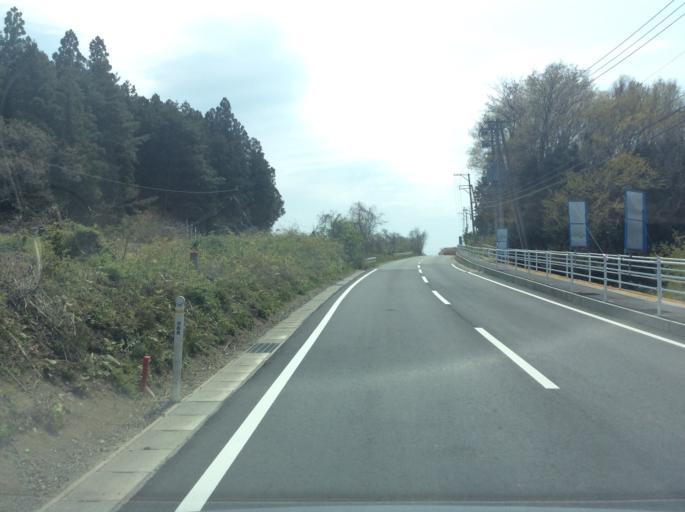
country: JP
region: Fukushima
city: Namie
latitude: 37.3716
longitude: 140.9915
